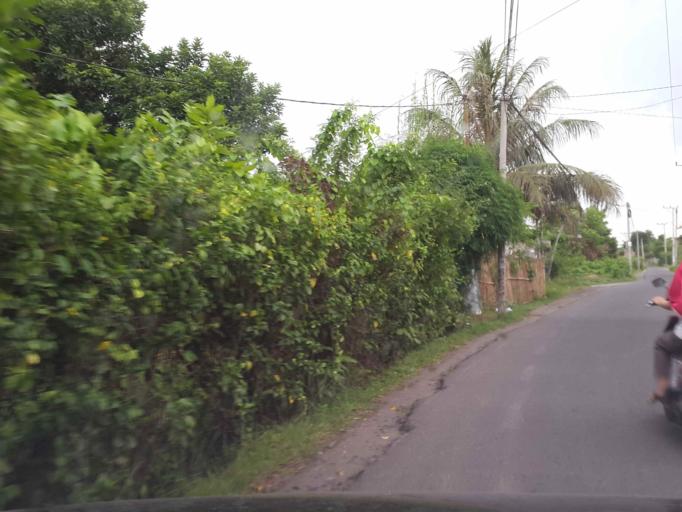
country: ID
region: West Nusa Tenggara
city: Kekeri
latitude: -8.5556
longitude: 116.1140
